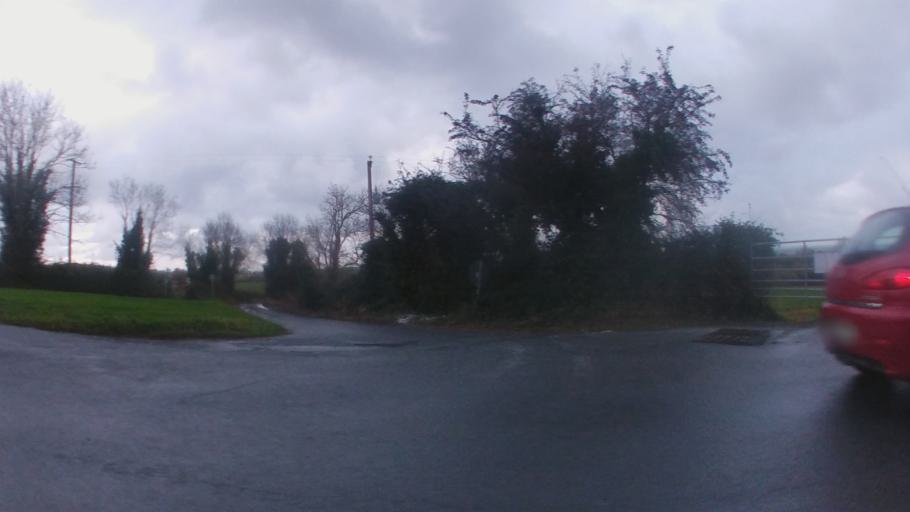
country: IE
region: Leinster
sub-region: Wicklow
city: Kilcoole
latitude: 53.1138
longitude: -6.0598
